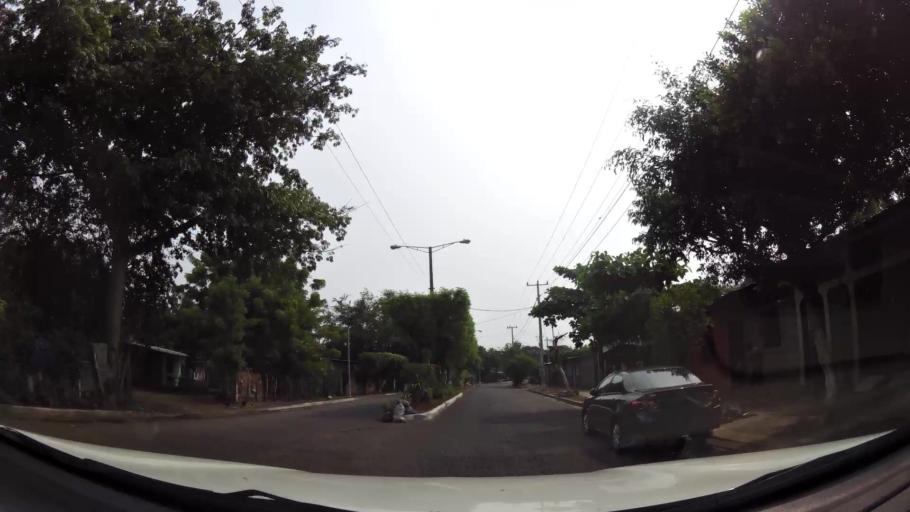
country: NI
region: Chinandega
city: Chinandega
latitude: 12.6286
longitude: -87.1405
